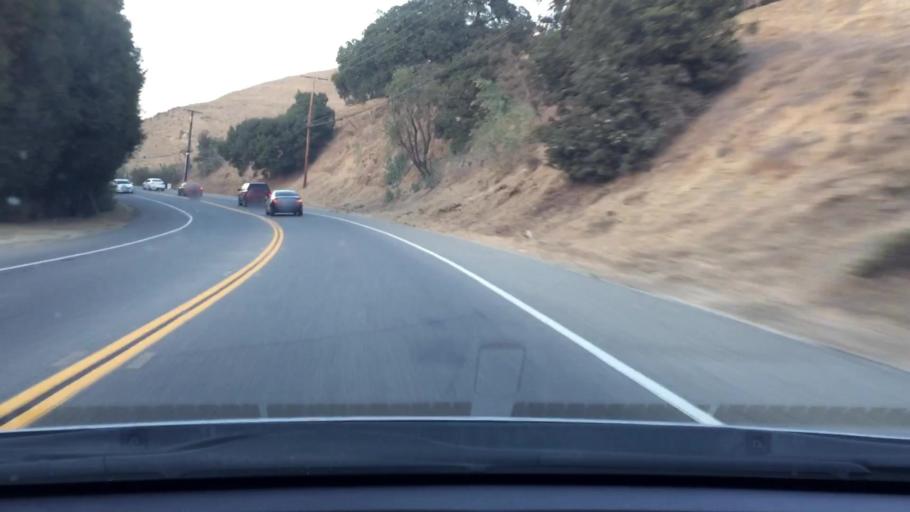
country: US
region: California
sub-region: San Bernardino County
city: Chino Hills
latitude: 33.9713
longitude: -117.7481
